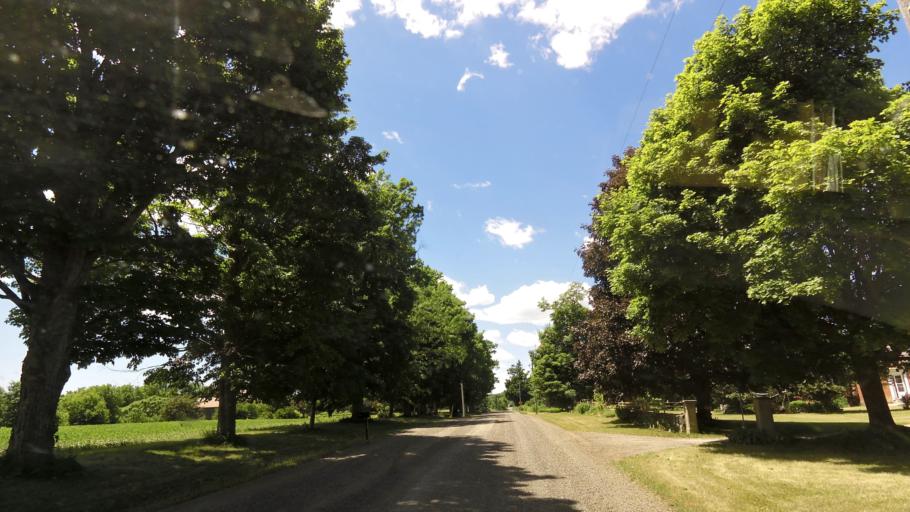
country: CA
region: Ontario
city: Omemee
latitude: 43.9944
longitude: -78.5117
